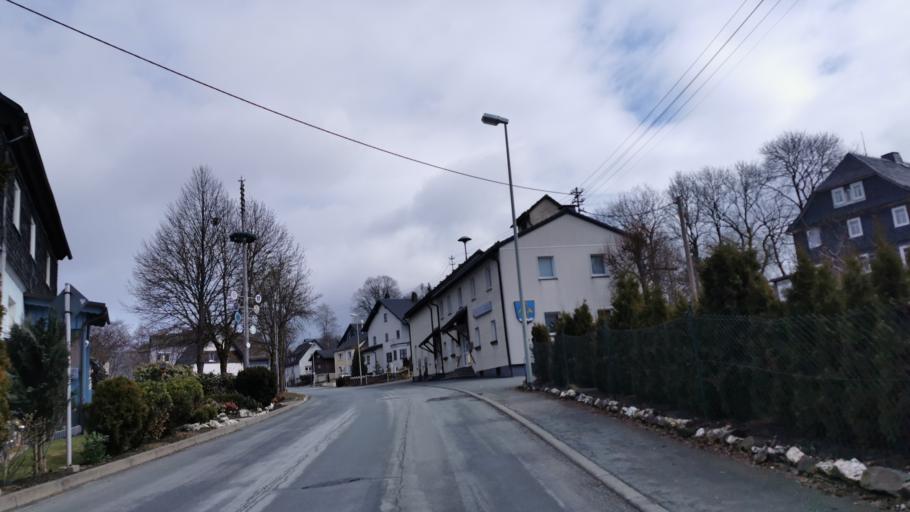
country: DE
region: Bavaria
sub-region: Upper Franconia
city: Reichenbach
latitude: 50.4248
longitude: 11.4139
